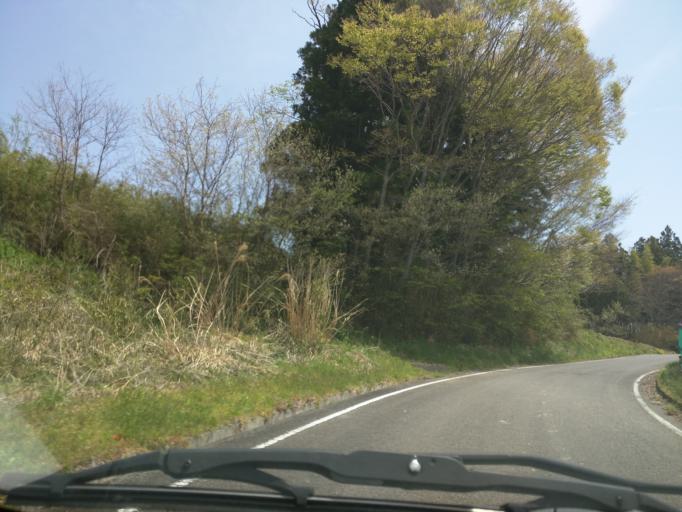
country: JP
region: Fukushima
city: Nihommatsu
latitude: 37.5435
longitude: 140.5082
